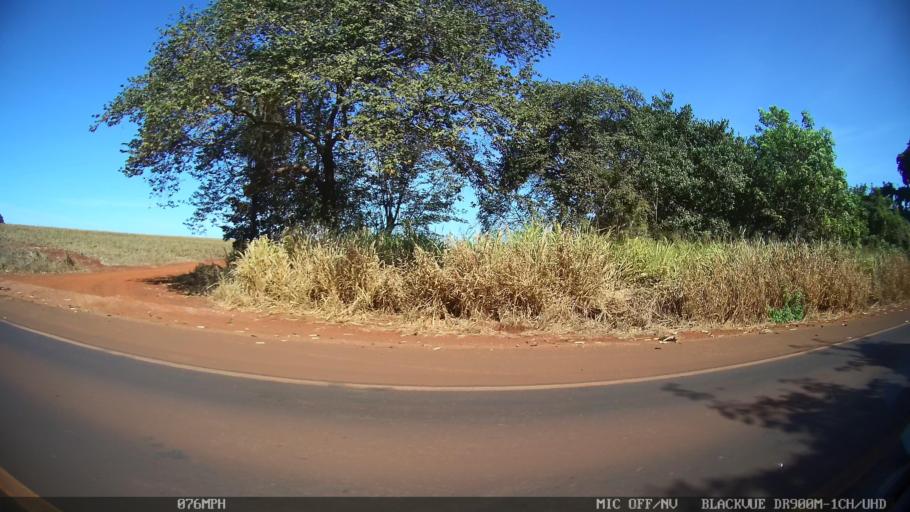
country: BR
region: Sao Paulo
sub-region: Guaira
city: Guaira
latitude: -20.4451
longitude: -48.3882
